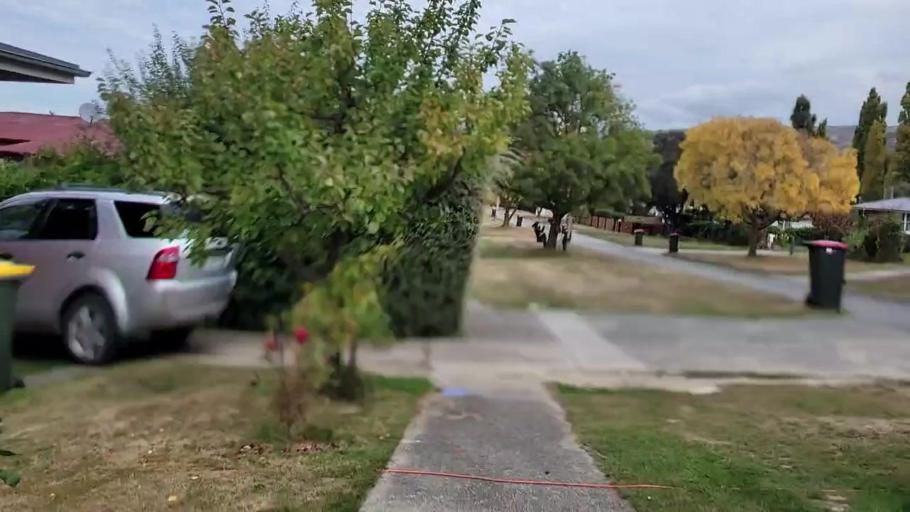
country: NZ
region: Otago
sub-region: Queenstown-Lakes District
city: Kingston
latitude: -45.4782
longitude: 169.3135
